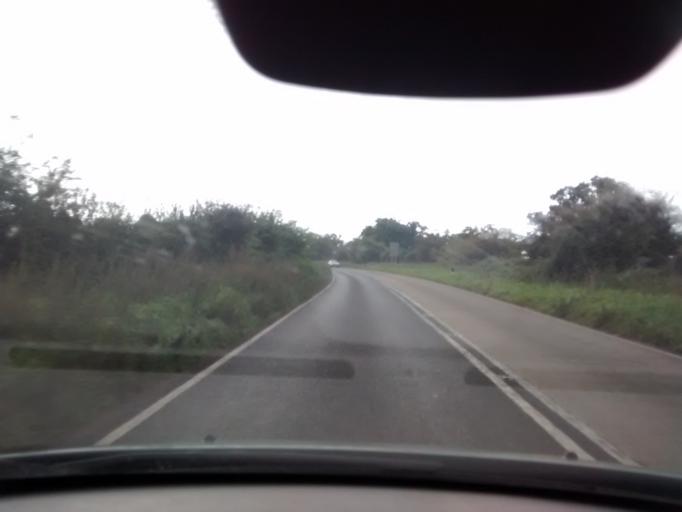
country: GB
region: England
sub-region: Hampshire
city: Fordingbridge
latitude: 50.8935
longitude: -1.7851
